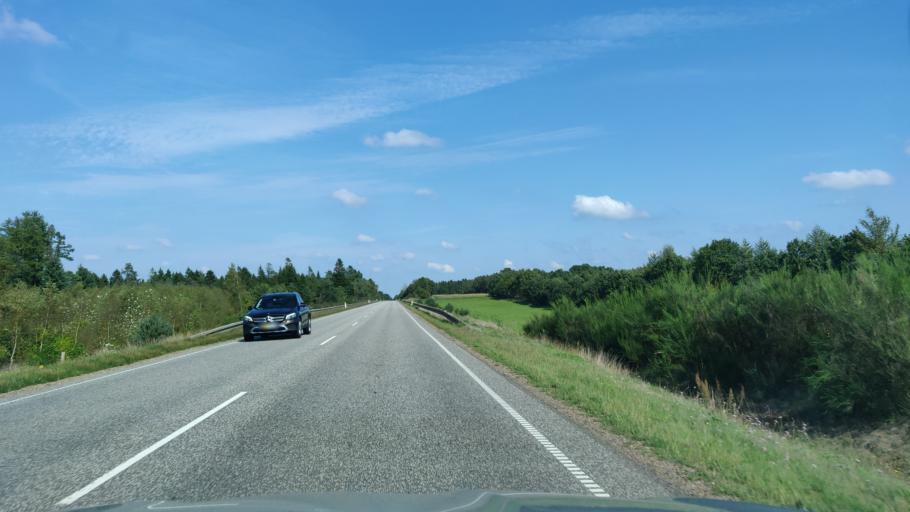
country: DK
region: Central Jutland
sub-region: Herning Kommune
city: Sunds
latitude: 56.3673
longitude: 8.9797
